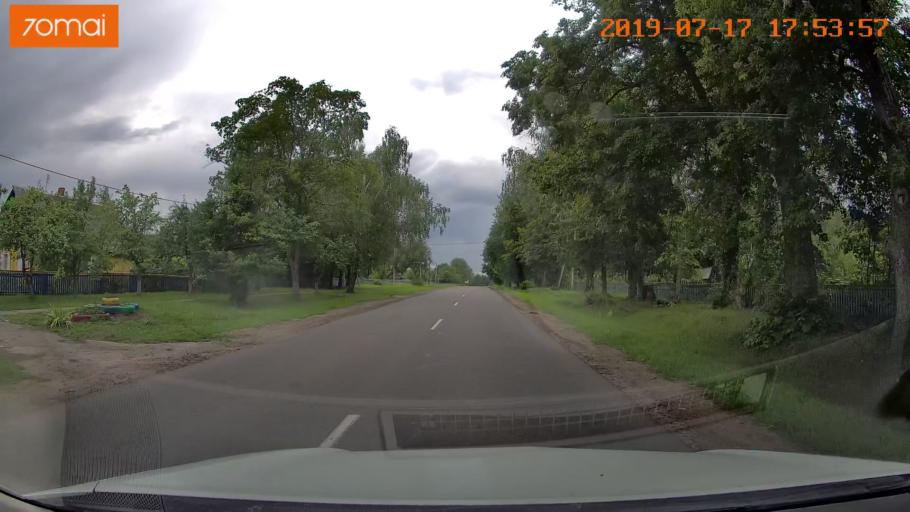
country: BY
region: Mogilev
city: Hlusha
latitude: 53.1730
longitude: 28.7622
